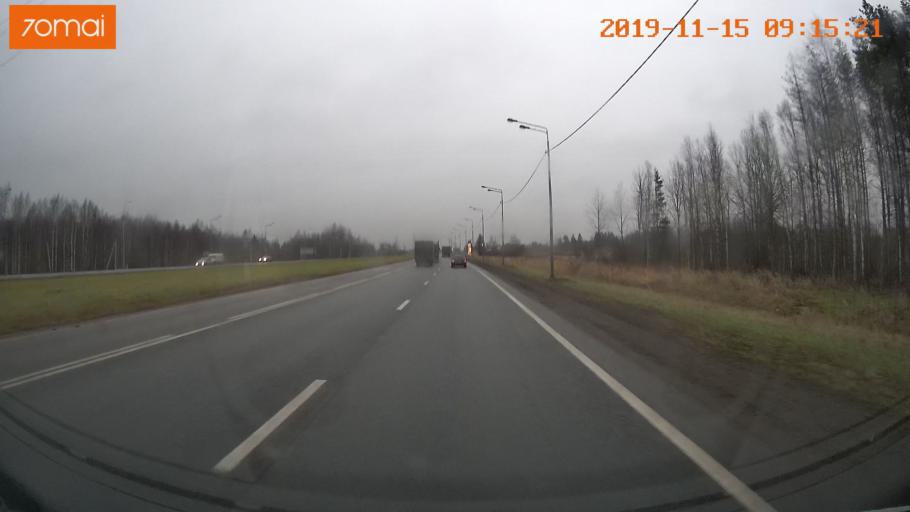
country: RU
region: Vologda
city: Tonshalovo
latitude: 59.2378
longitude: 37.9664
